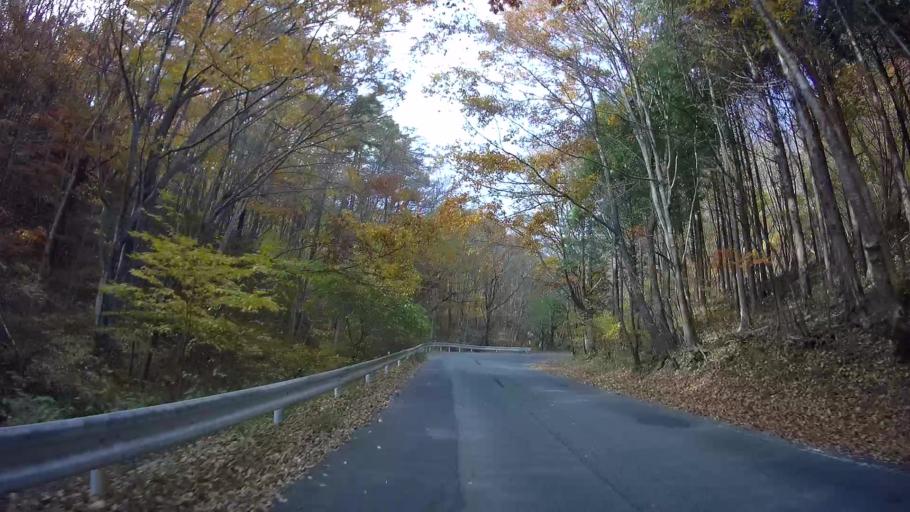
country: JP
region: Gunma
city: Nakanojomachi
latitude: 36.5159
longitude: 138.6683
